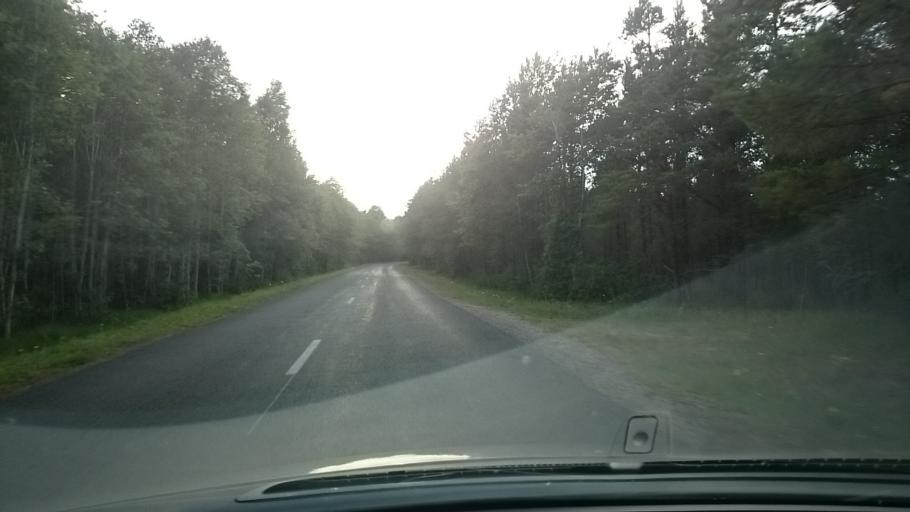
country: EE
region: Saare
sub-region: Kuressaare linn
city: Kuressaare
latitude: 58.4158
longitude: 22.0838
